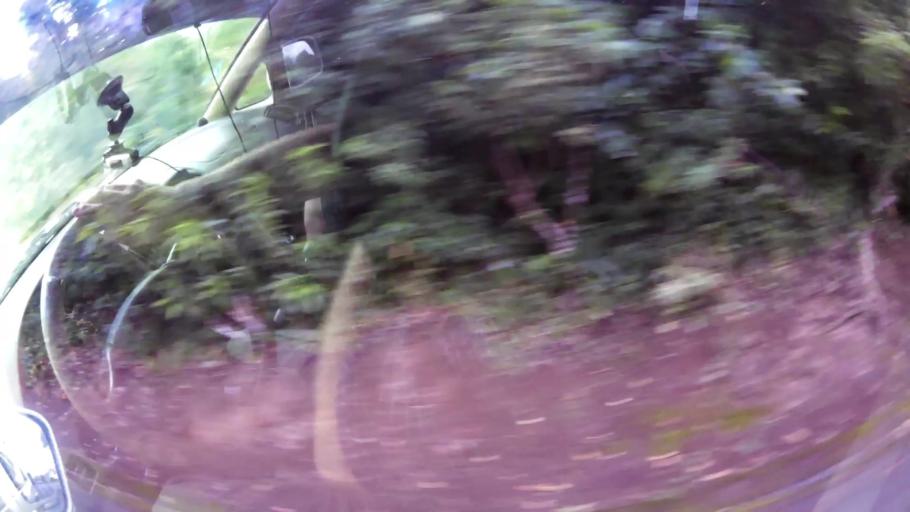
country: VC
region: Saint George
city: Kingstown
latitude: 13.1652
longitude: -61.1771
